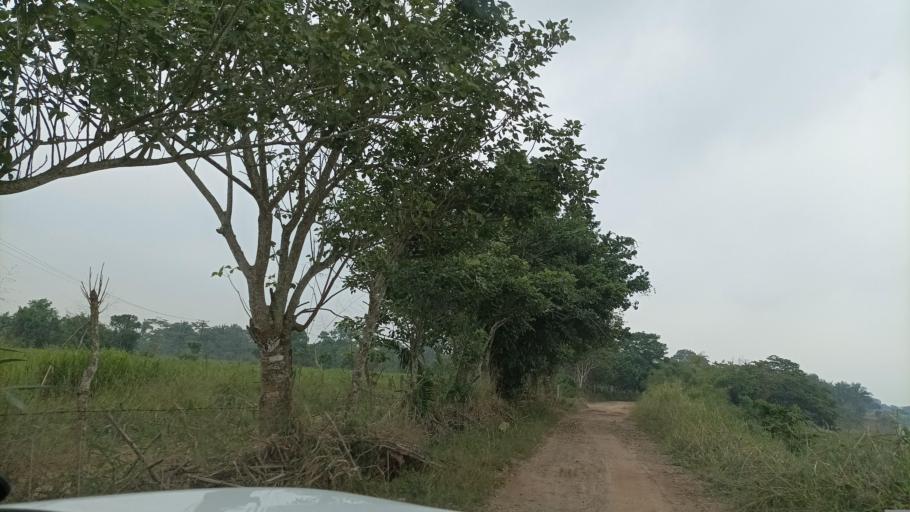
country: MX
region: Veracruz
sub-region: Uxpanapa
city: Poblado 10
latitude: 17.5591
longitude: -94.2261
